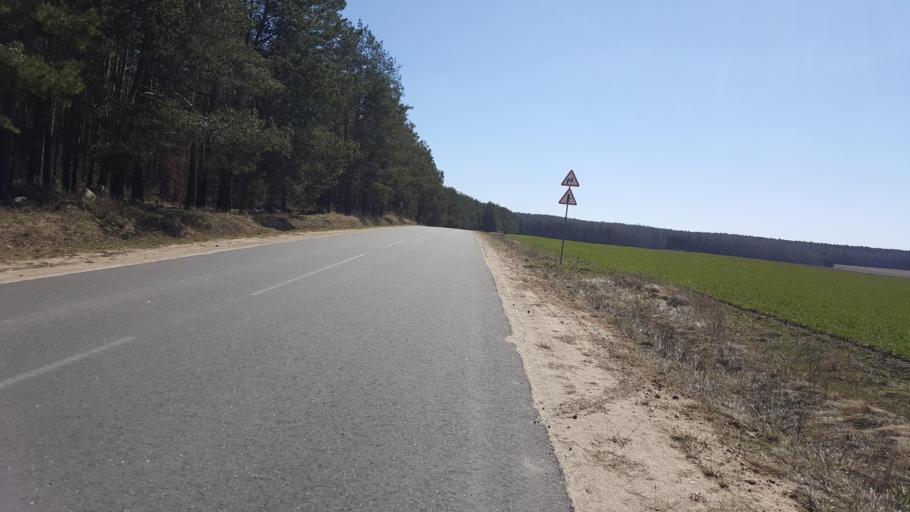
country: BY
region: Brest
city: Kamyanyets
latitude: 52.3651
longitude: 23.8077
